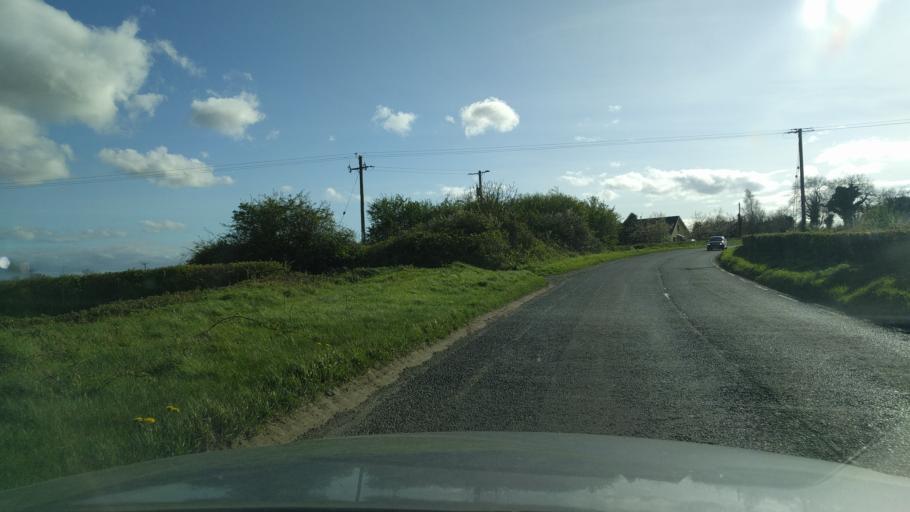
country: IE
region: Leinster
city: Balrothery
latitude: 53.6013
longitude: -6.2119
